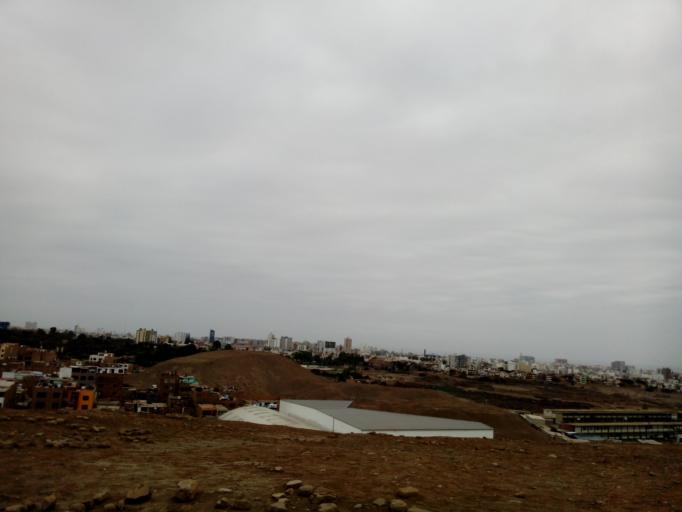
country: PE
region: Callao
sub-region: Callao
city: Callao
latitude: -12.0609
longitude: -77.0867
